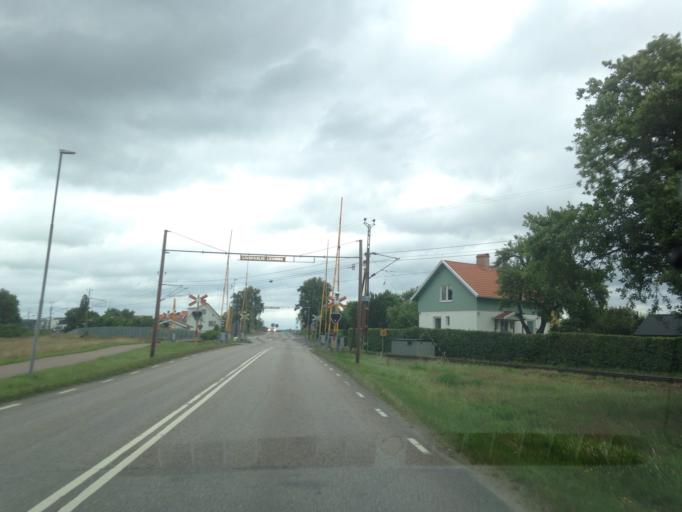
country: SE
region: Vaestra Goetaland
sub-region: Kungalvs Kommun
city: Kungalv
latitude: 57.8556
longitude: 11.9148
